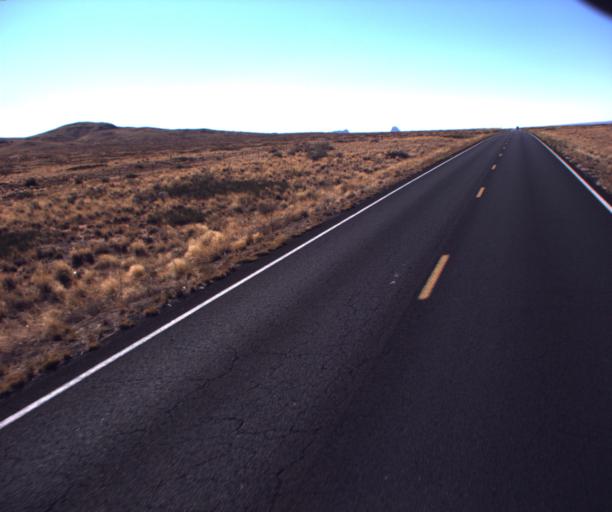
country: US
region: Arizona
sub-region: Navajo County
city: Dilkon
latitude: 35.4242
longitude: -110.4262
